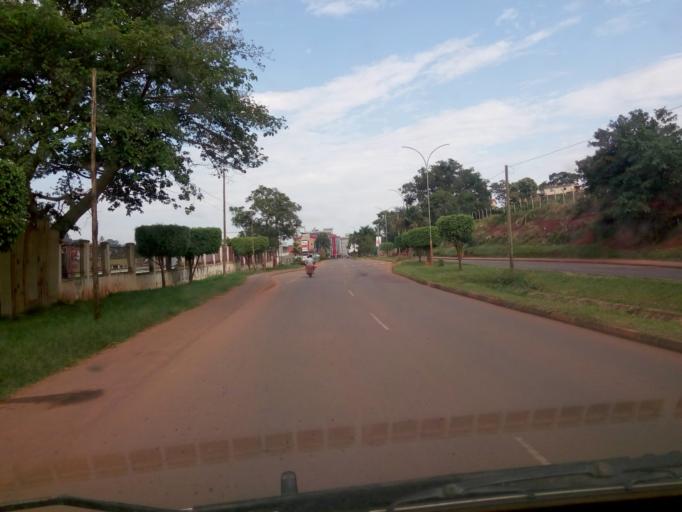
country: UG
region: Central Region
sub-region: Kampala District
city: Kampala
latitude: 0.3381
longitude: 32.5994
